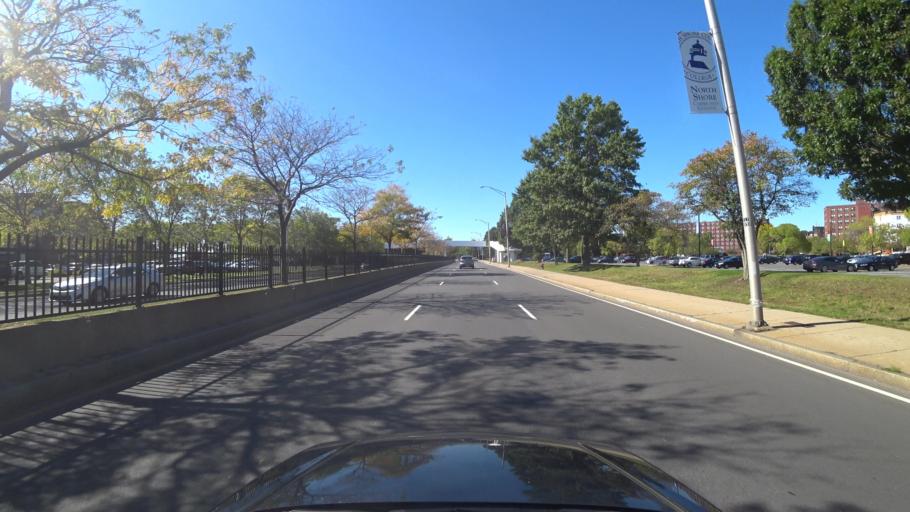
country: US
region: Massachusetts
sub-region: Essex County
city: Lynn
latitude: 42.4592
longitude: -70.9415
